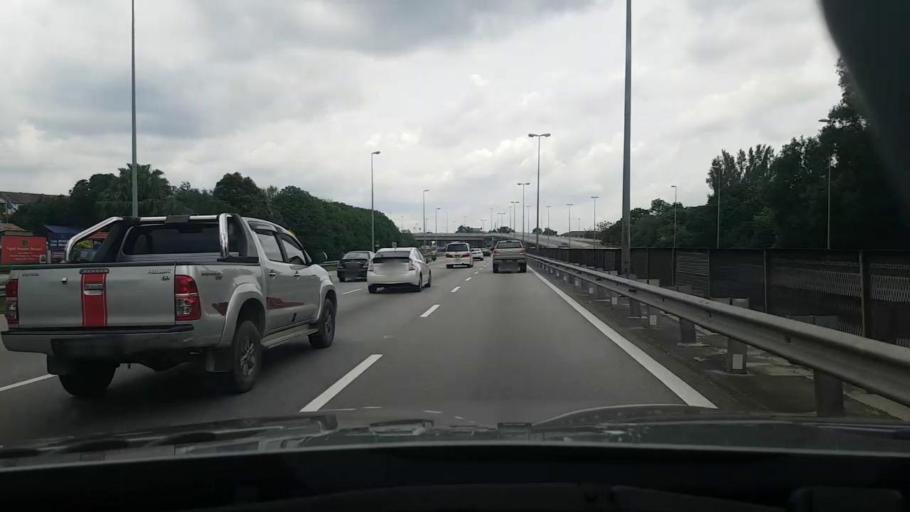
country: MY
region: Selangor
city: Subang Jaya
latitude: 2.9962
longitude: 101.6145
